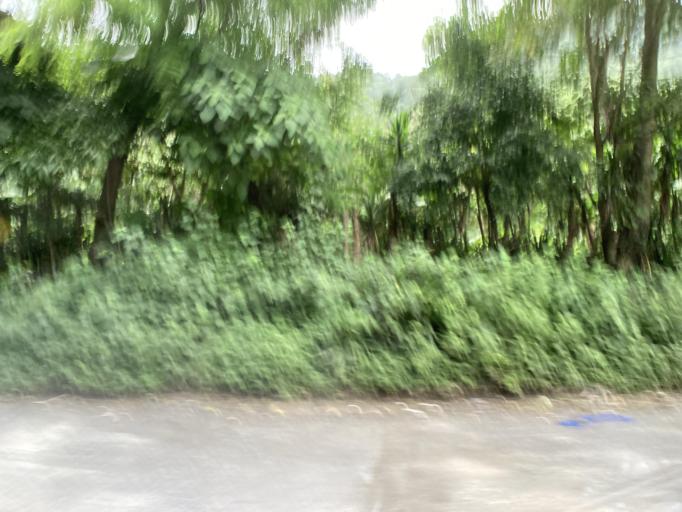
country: GT
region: Guatemala
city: Villa Canales
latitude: 14.4212
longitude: -90.5371
